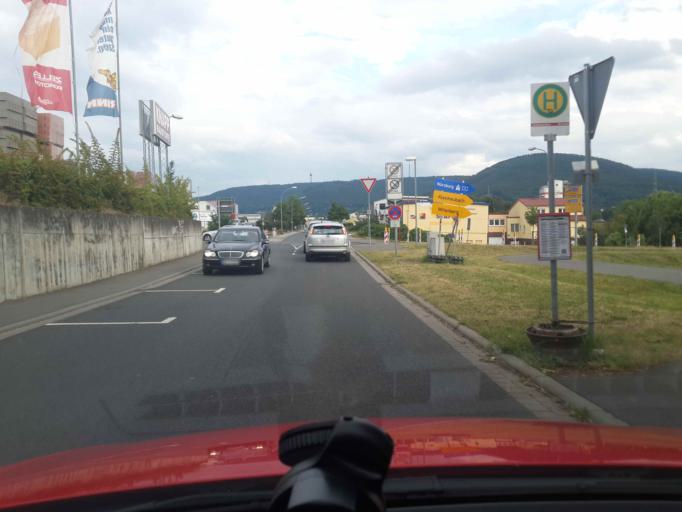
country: DE
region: Bavaria
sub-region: Regierungsbezirk Unterfranken
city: Grossheubach
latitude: 49.7210
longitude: 9.2280
